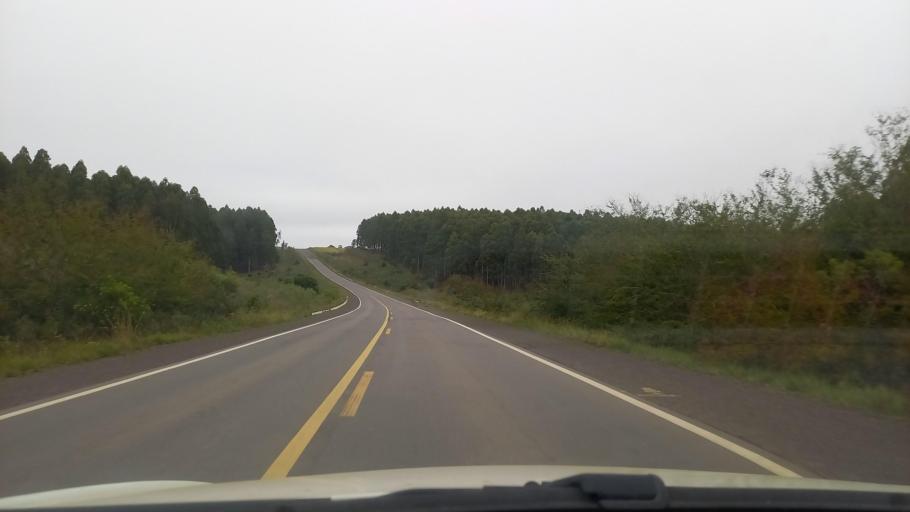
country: BR
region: Rio Grande do Sul
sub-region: Cacequi
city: Cacequi
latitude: -30.0399
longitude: -54.5918
